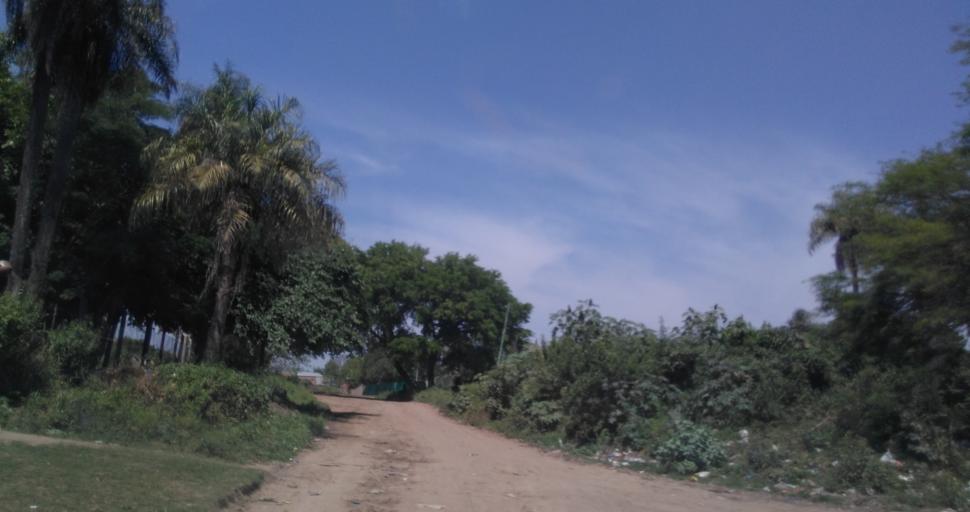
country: AR
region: Chaco
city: Fontana
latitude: -27.4228
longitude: -59.0137
